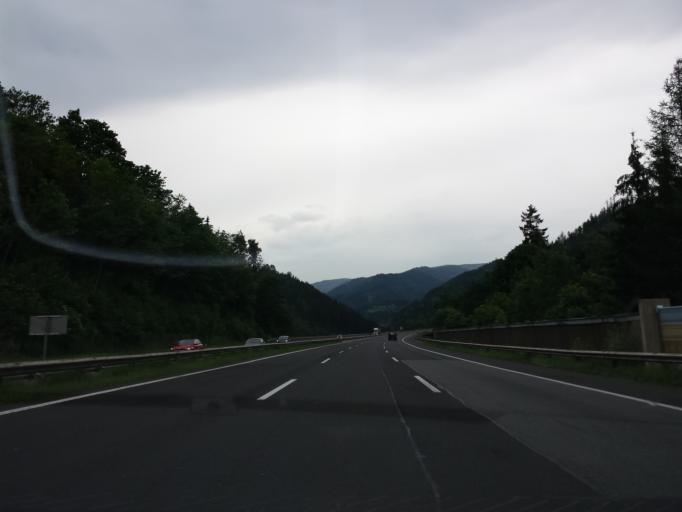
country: AT
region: Styria
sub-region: Politischer Bezirk Graz-Umgebung
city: Ubelbach
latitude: 47.2285
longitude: 15.2200
